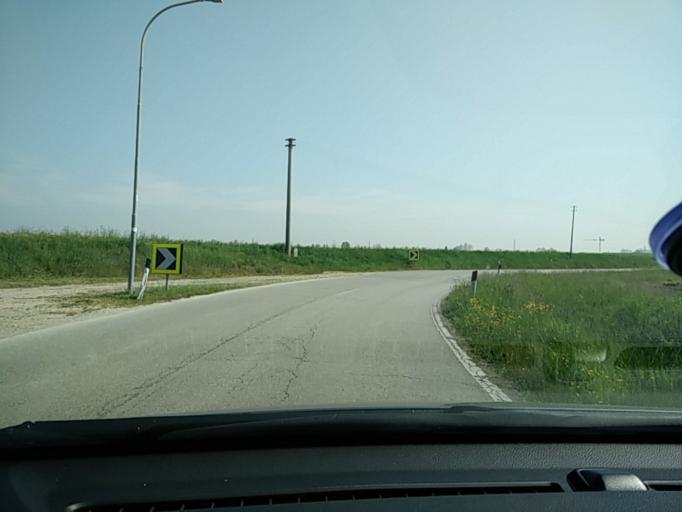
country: IT
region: Veneto
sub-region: Provincia di Treviso
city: Zenson di Piave
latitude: 45.6768
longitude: 12.4681
